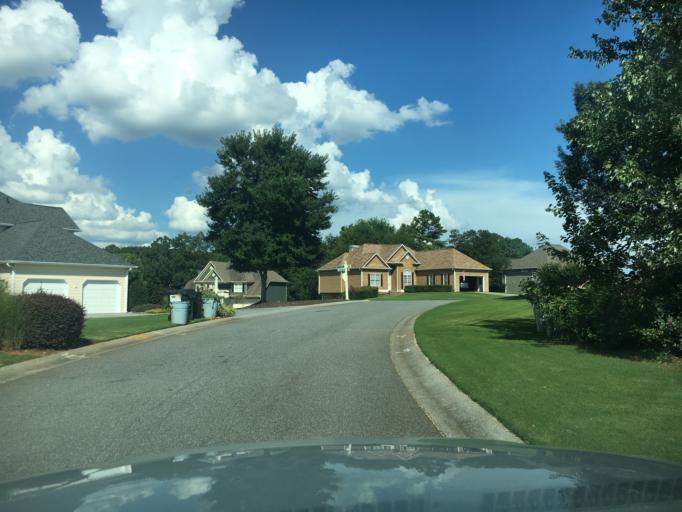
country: US
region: Georgia
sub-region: Cherokee County
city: Holly Springs
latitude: 34.1508
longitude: -84.4613
